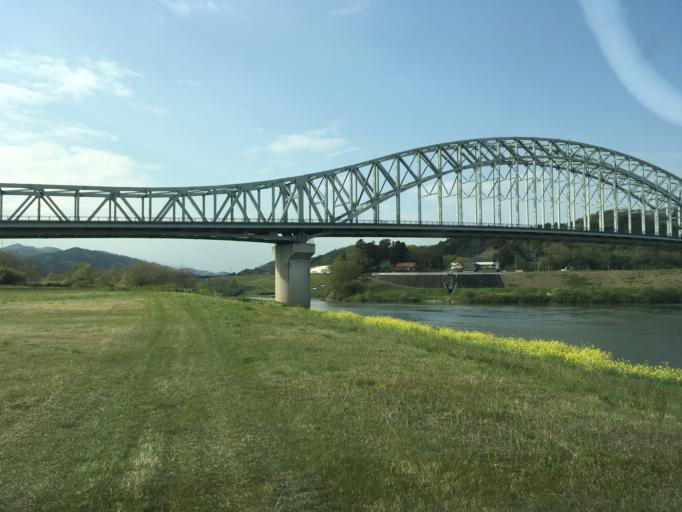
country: JP
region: Iwate
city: Ichinoseki
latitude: 38.8967
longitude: 141.2630
